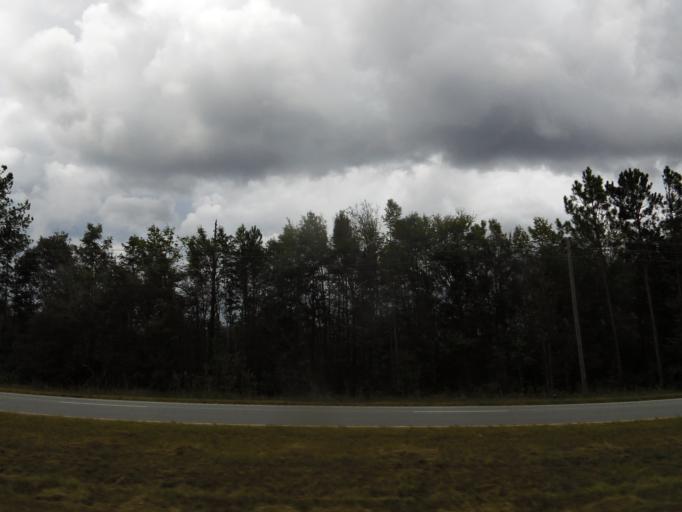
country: US
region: Georgia
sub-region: Brantley County
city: Nahunta
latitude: 31.2131
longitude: -81.9192
